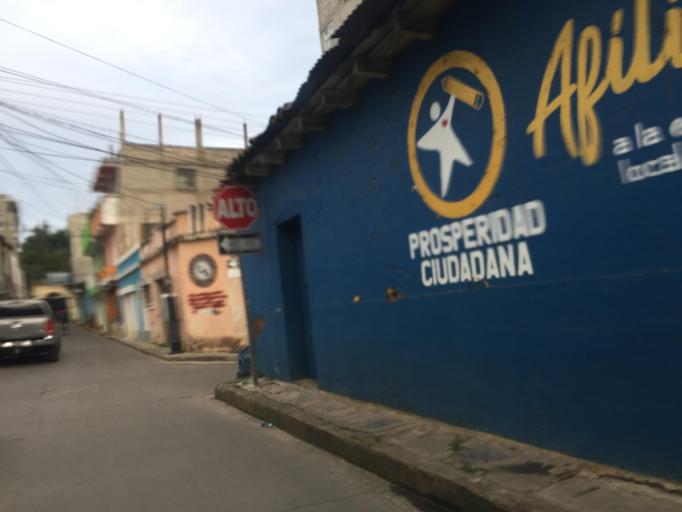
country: GT
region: Totonicapan
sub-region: Municipio de Totonicapan
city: Totonicapan
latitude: 14.9096
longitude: -91.3626
